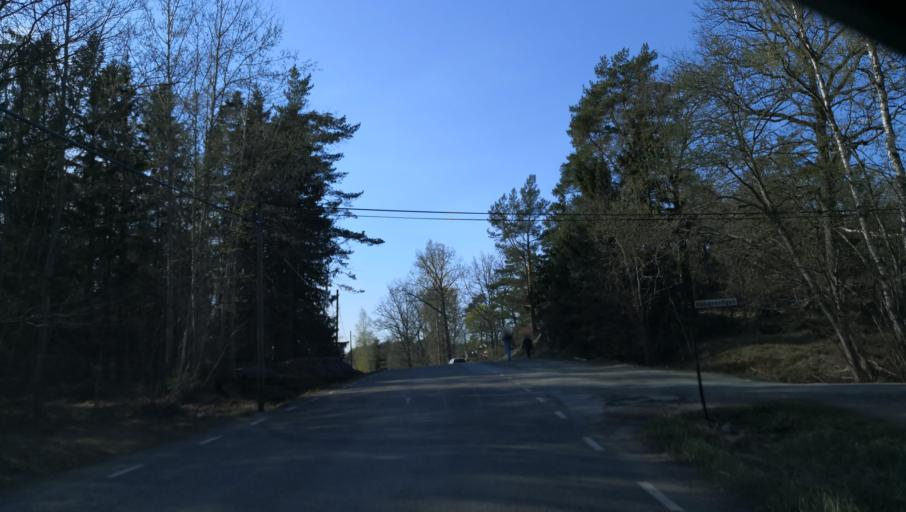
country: SE
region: Stockholm
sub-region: Varmdo Kommun
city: Holo
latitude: 59.2974
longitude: 18.6106
